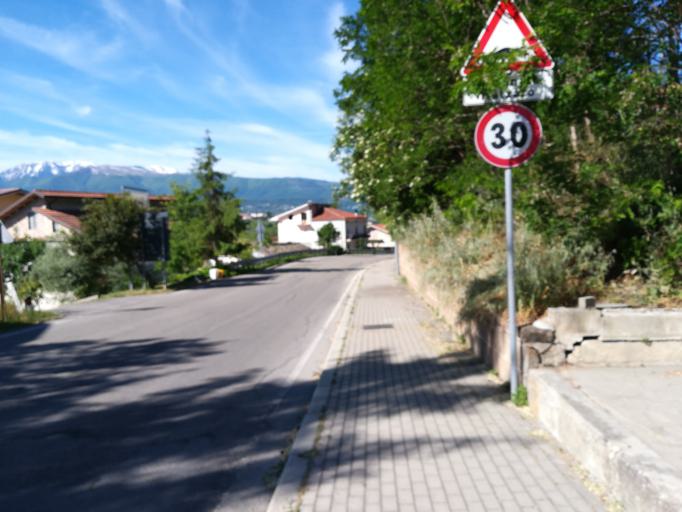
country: IT
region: Abruzzo
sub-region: Provincia di Chieti
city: Bucchianico
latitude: 42.3011
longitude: 14.1808
